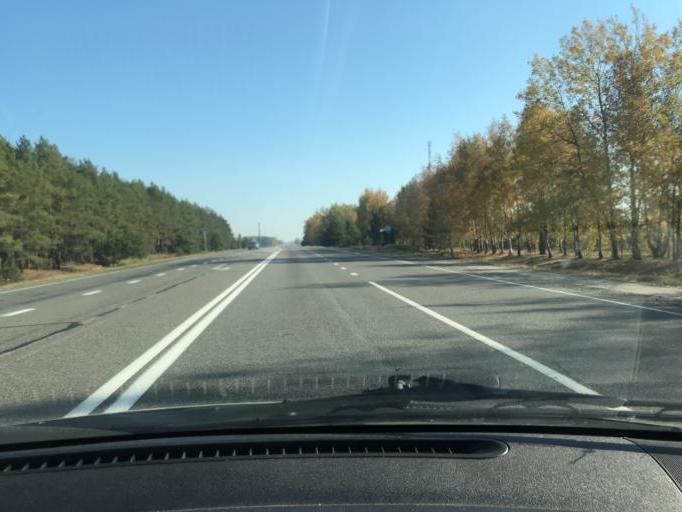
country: BY
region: Brest
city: Davyd-Haradok
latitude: 52.2447
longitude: 27.1402
